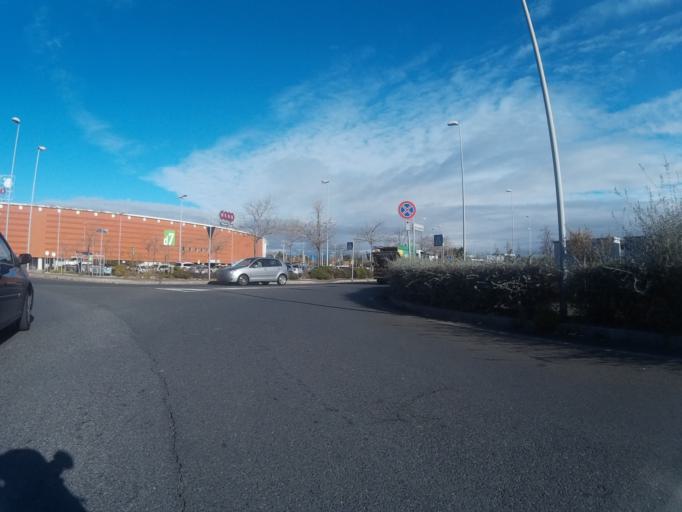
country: IT
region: Tuscany
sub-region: Provincia di Livorno
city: Livorno
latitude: 43.5493
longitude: 10.3398
